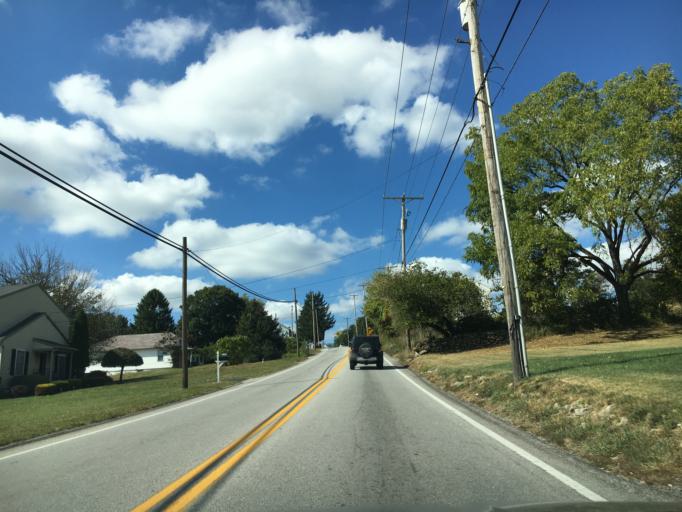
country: US
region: Pennsylvania
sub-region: York County
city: East York
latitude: 40.0000
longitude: -76.6801
